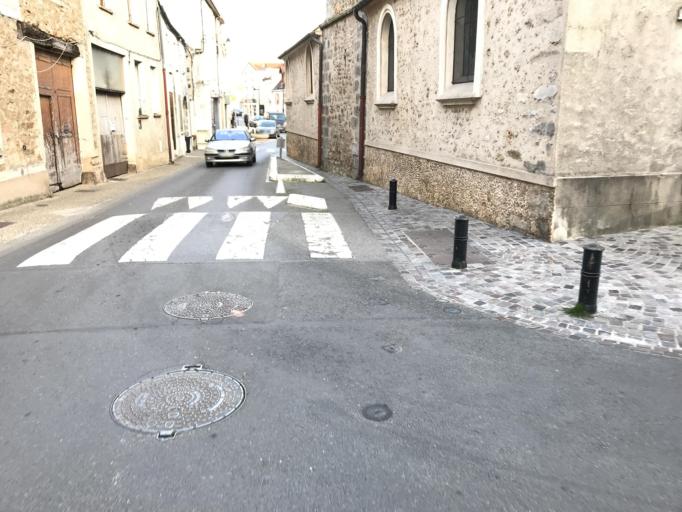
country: FR
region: Ile-de-France
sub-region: Departement de l'Essonne
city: La Ville-du-Bois
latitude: 48.6611
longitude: 2.2675
